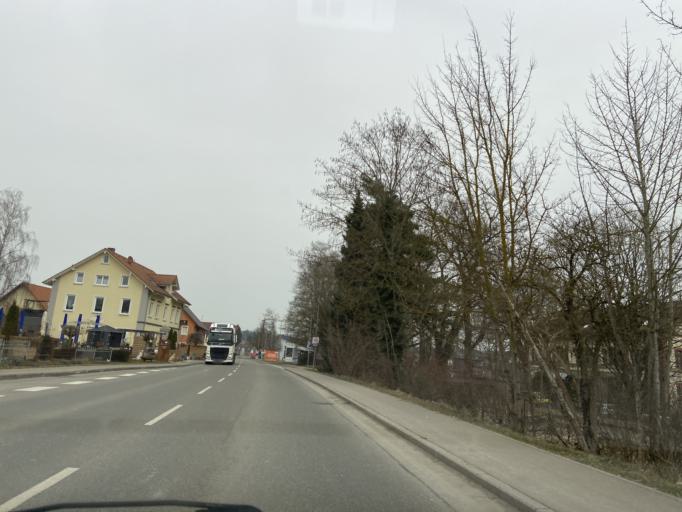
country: DE
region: Baden-Wuerttemberg
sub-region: Tuebingen Region
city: Ostrach
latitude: 47.9464
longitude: 9.3779
